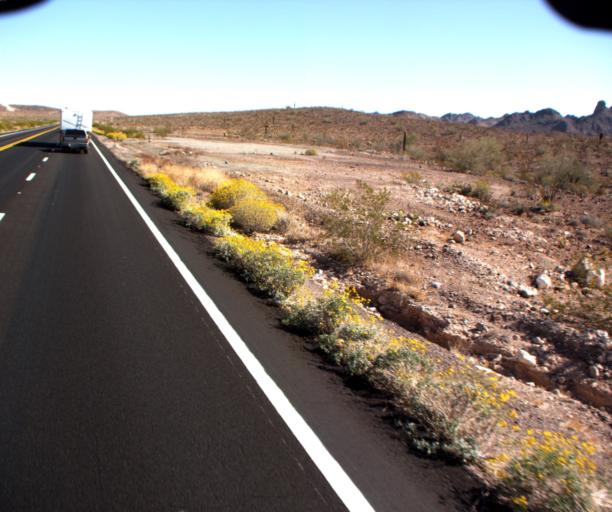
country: US
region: Arizona
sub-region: La Paz County
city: Quartzsite
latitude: 33.2242
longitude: -114.2569
